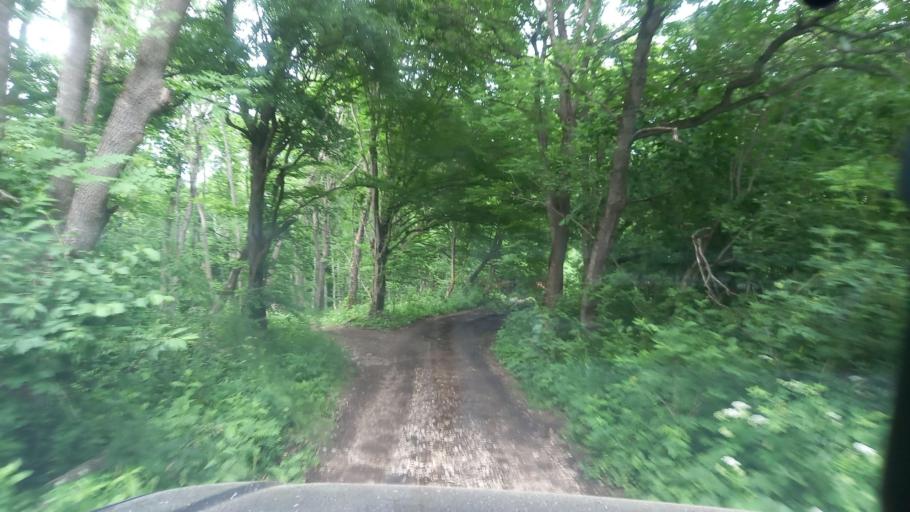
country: RU
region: Karachayevo-Cherkesiya
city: Pregradnaya
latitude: 44.0259
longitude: 41.2990
